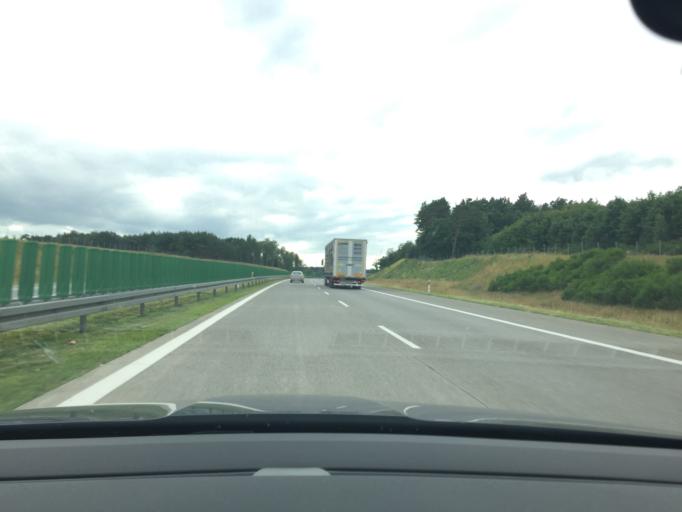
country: PL
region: Lubusz
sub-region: Powiat miedzyrzecki
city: Brojce
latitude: 52.2983
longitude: 15.6651
